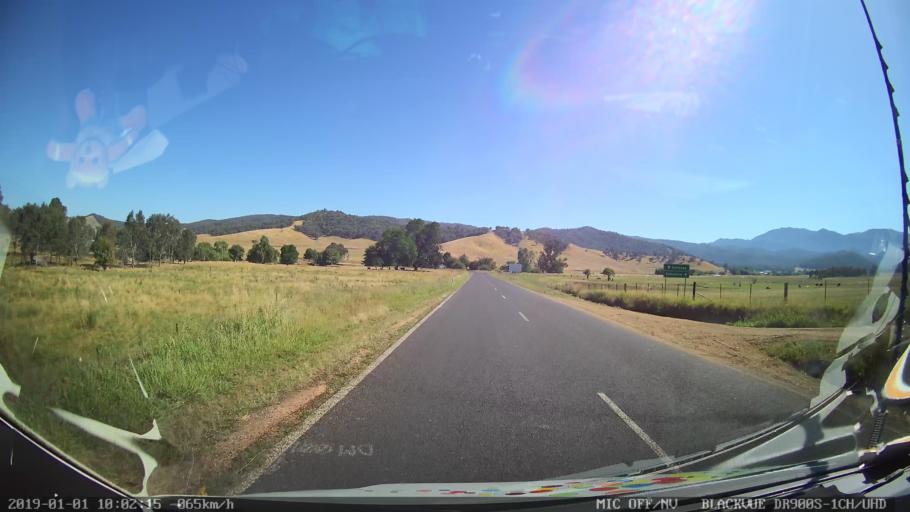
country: AU
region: New South Wales
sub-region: Snowy River
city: Jindabyne
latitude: -36.1831
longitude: 148.1017
